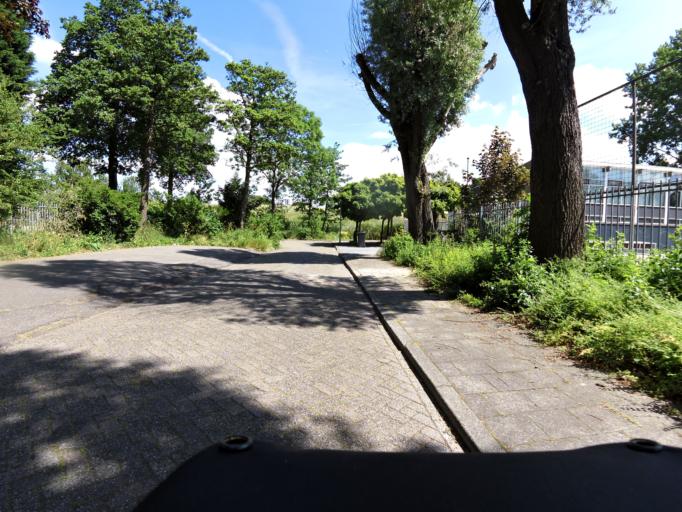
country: NL
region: South Holland
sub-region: Gemeente Maassluis
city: Maassluis
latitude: 51.8995
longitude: 4.2623
